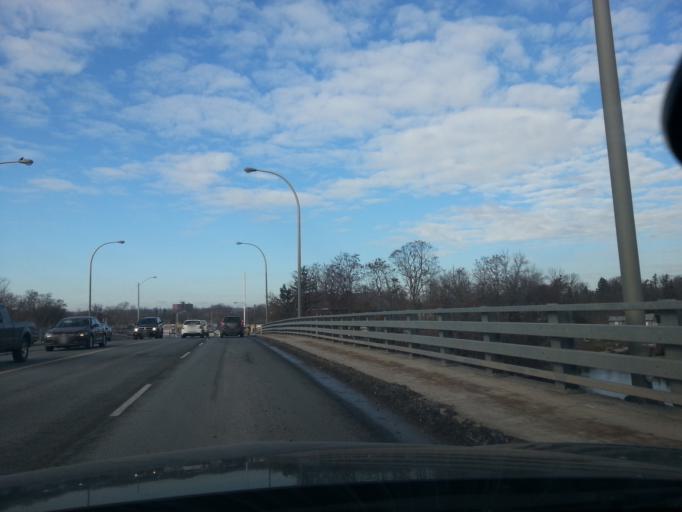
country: CA
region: Ontario
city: Peterborough
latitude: 44.2897
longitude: -78.3067
